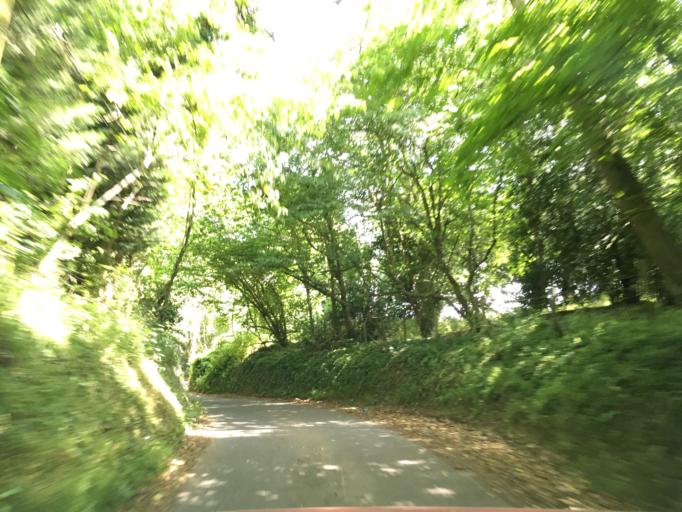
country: GB
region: Wales
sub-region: Monmouthshire
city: Magor
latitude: 51.6024
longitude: -2.8445
